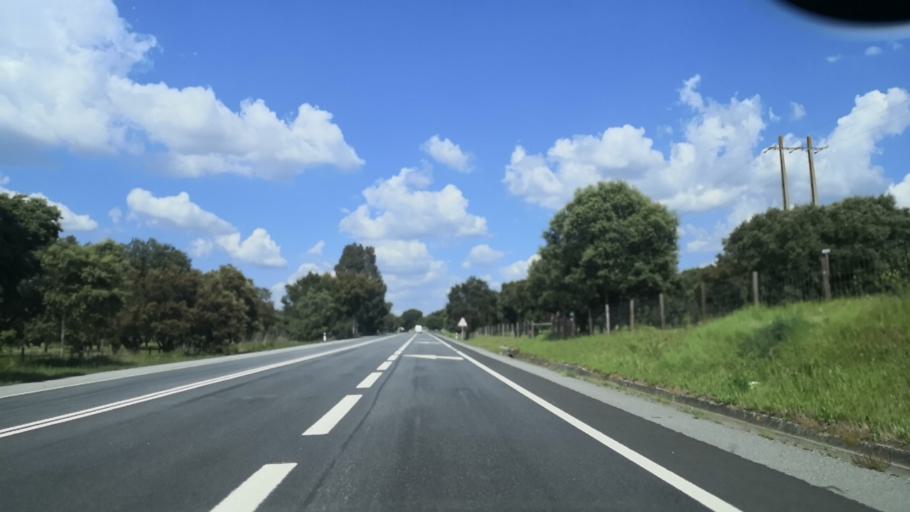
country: PT
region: Evora
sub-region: Montemor-O-Novo
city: Montemor-o-Novo
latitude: 38.6778
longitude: -8.1340
